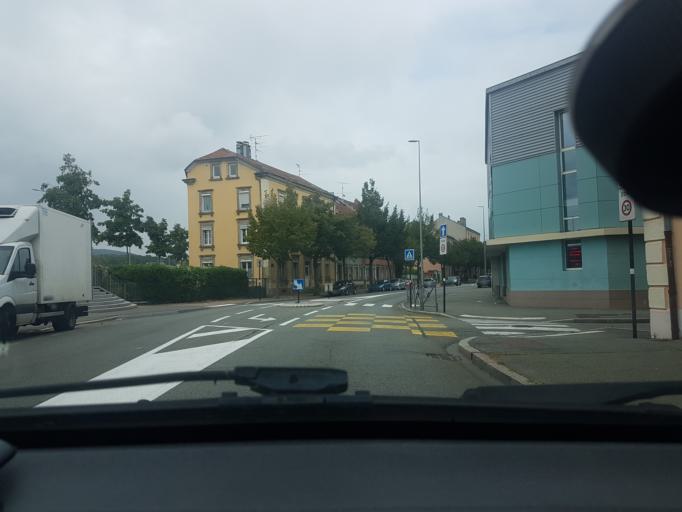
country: FR
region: Franche-Comte
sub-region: Territoire de Belfort
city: Belfort
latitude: 47.6299
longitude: 6.8564
